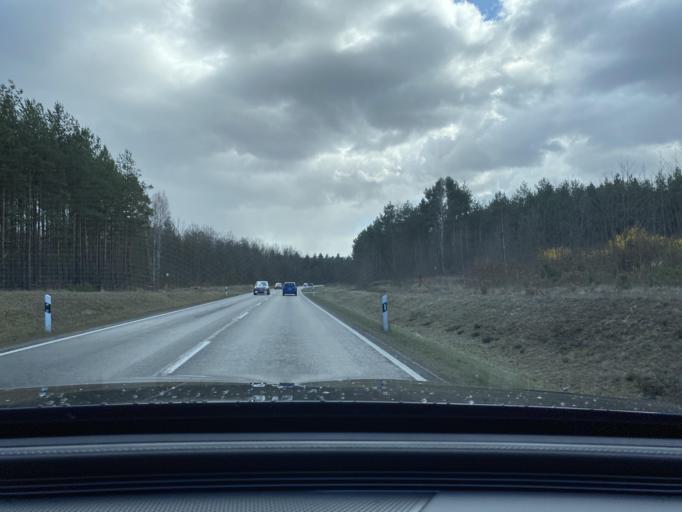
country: DE
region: Saxony
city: Weisskeissel
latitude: 51.4600
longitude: 14.6807
